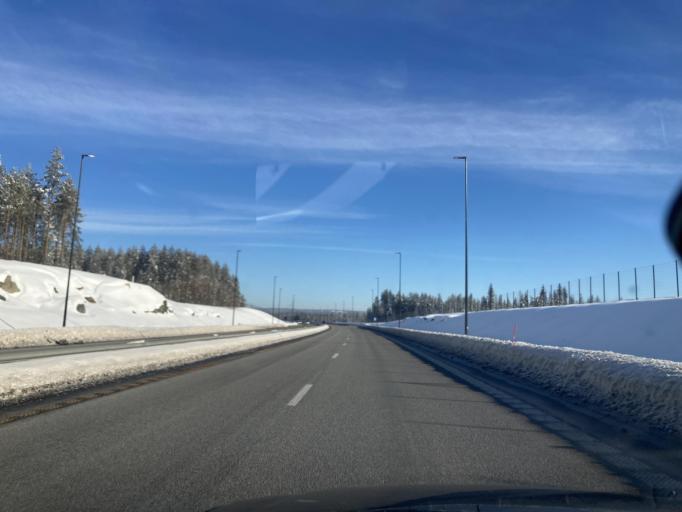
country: NO
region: Hedmark
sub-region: Loten
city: Loten
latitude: 60.8670
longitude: 11.4347
